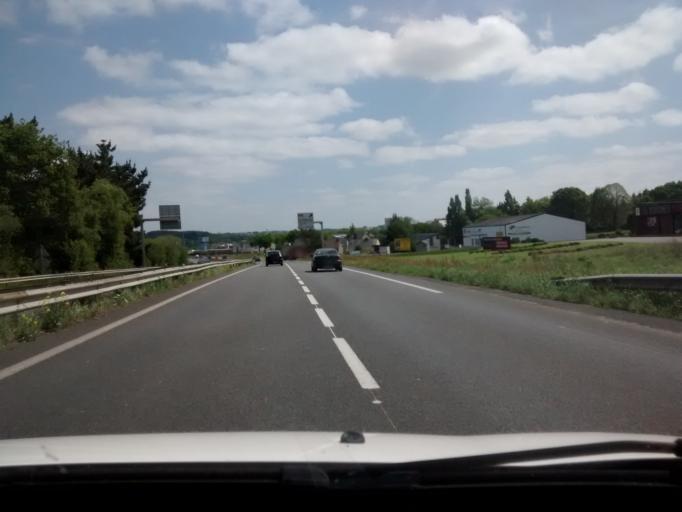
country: FR
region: Brittany
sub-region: Departement des Cotes-d'Armor
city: Graces
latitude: 48.5516
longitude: -3.1693
